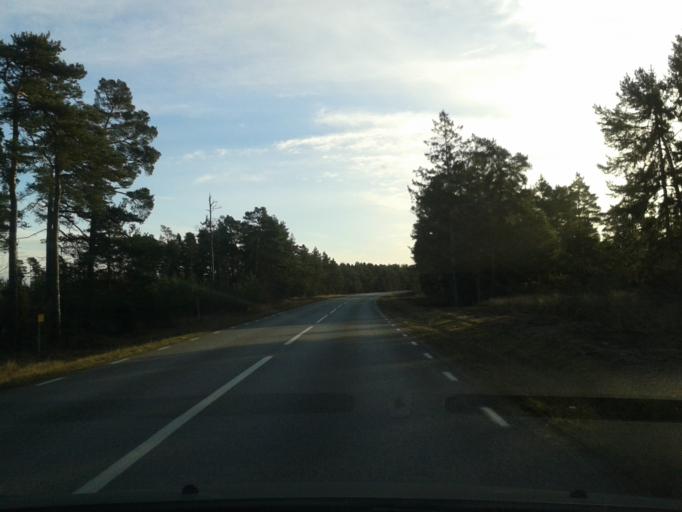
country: SE
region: Gotland
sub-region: Gotland
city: Hemse
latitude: 57.3478
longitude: 18.6910
